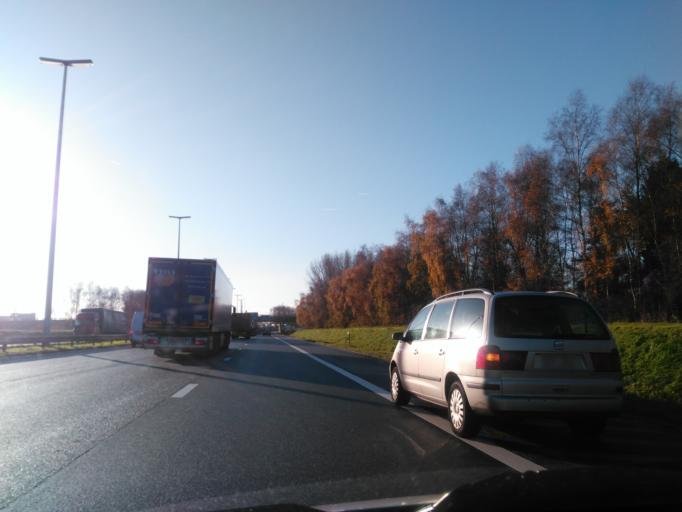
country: BE
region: Flanders
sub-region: Provincie Antwerpen
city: Zwijndrecht
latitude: 51.2227
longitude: 4.3518
